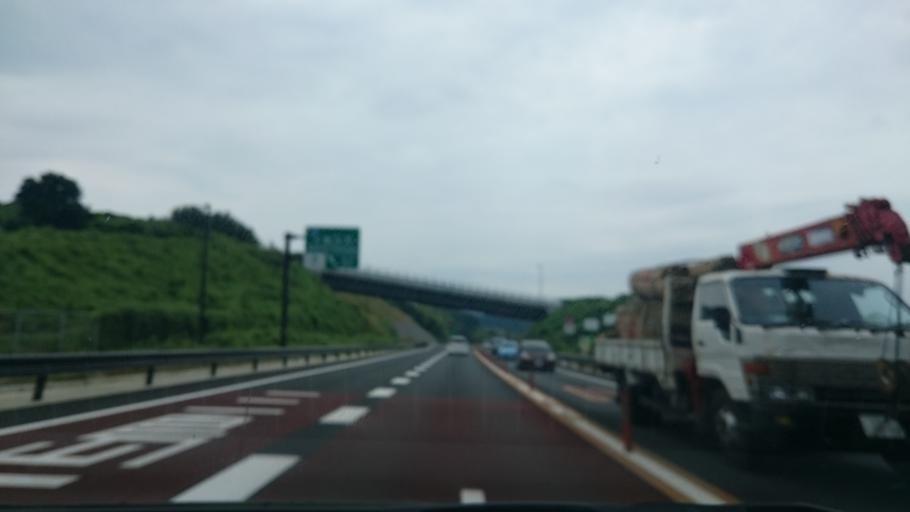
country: JP
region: Shizuoka
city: Mishima
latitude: 35.1250
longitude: 138.9471
